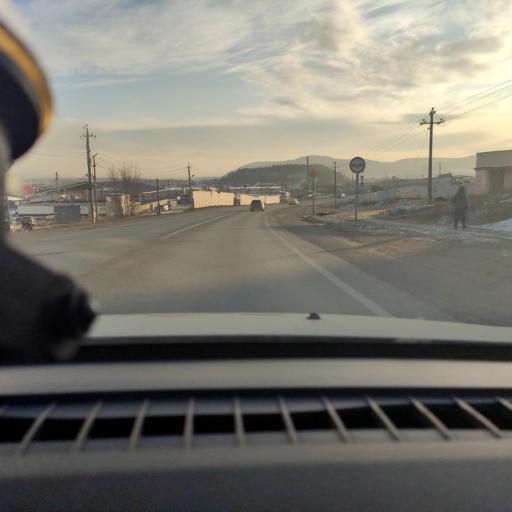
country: RU
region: Samara
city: Volzhskiy
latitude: 53.4366
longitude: 50.1249
